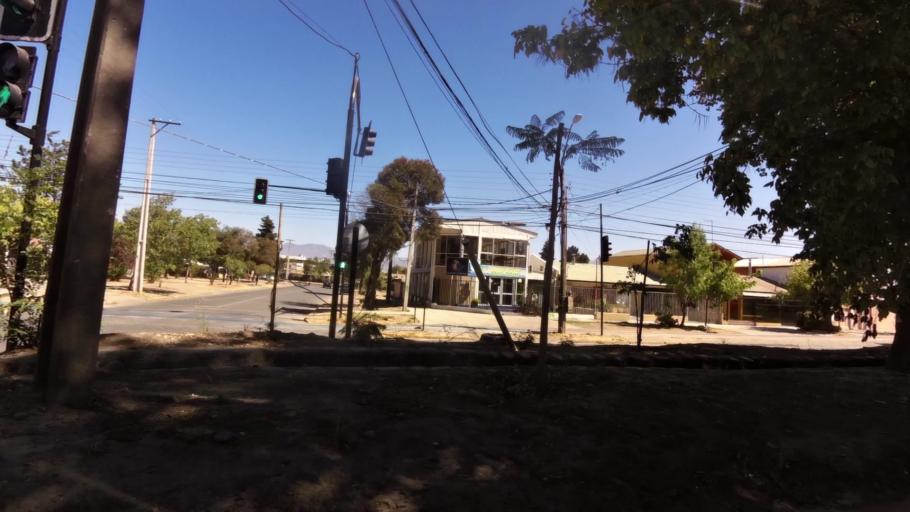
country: CL
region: O'Higgins
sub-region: Provincia de Cachapoal
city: Rancagua
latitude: -34.1780
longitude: -70.7153
